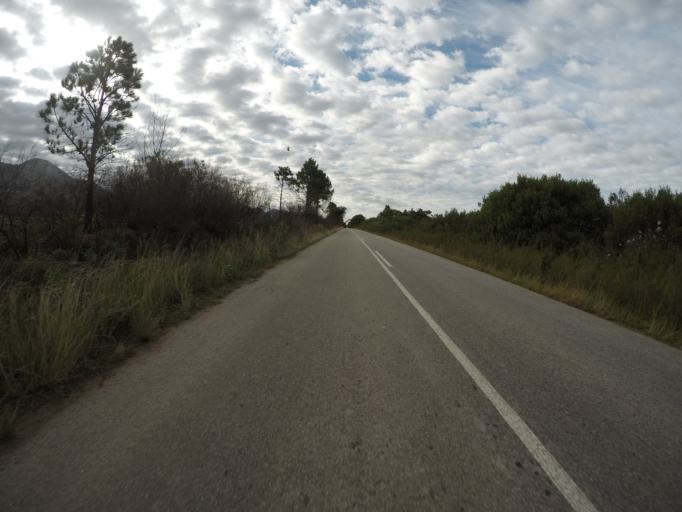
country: ZA
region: Eastern Cape
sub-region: Cacadu District Municipality
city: Kareedouw
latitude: -34.0433
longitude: 24.4243
